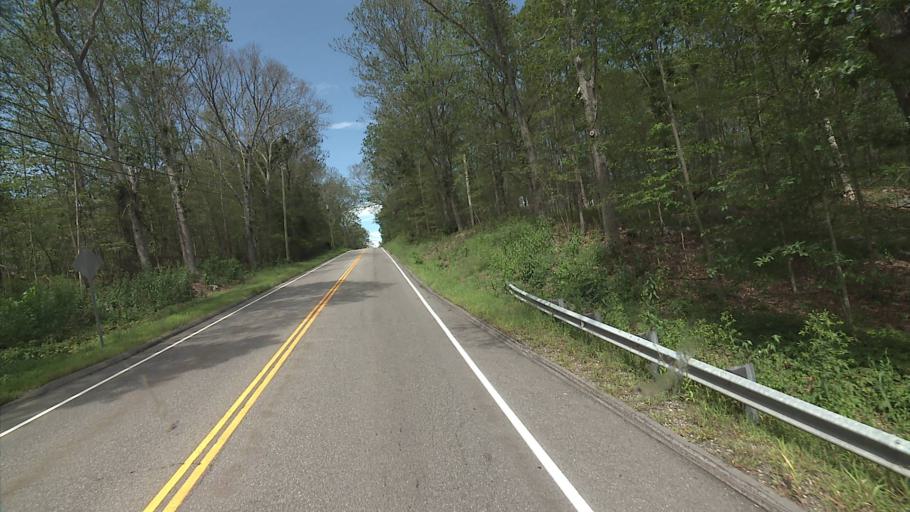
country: US
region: Connecticut
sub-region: Tolland County
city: Mansfield City
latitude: 41.7724
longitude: -72.2050
